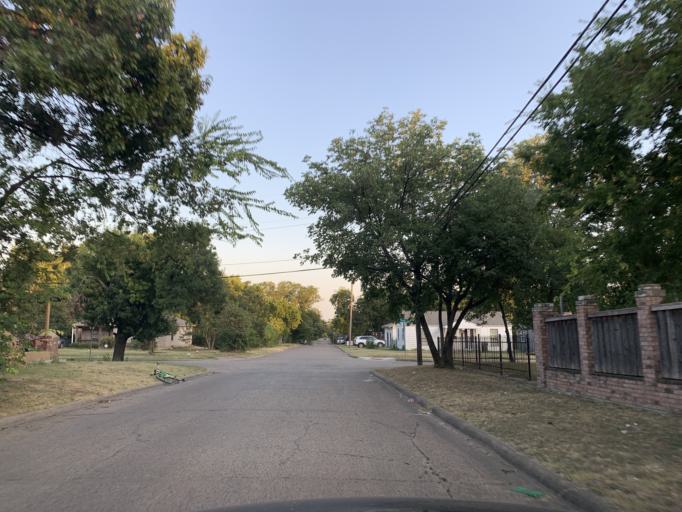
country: US
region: Texas
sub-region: Dallas County
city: Dallas
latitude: 32.7070
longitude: -96.8033
